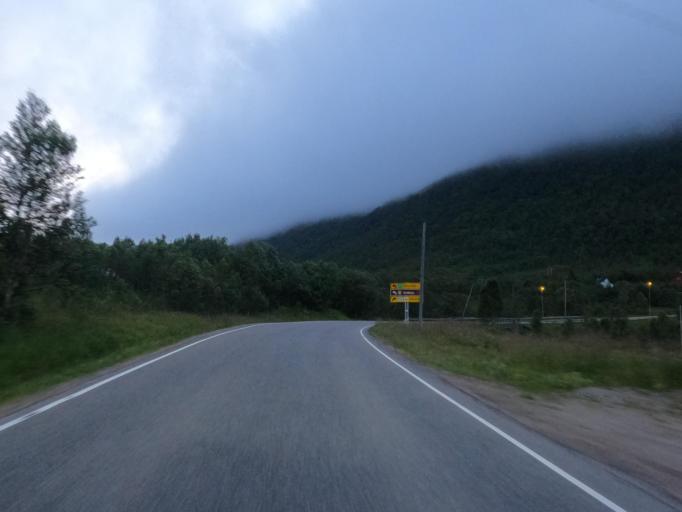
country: NO
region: Nordland
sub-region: Lodingen
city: Lodingen
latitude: 68.6154
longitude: 15.7617
